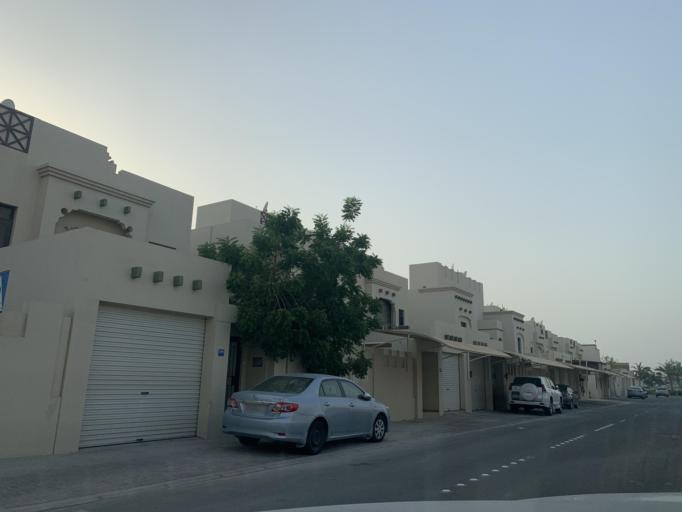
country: BH
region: Manama
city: Jidd Hafs
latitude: 26.2211
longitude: 50.4419
